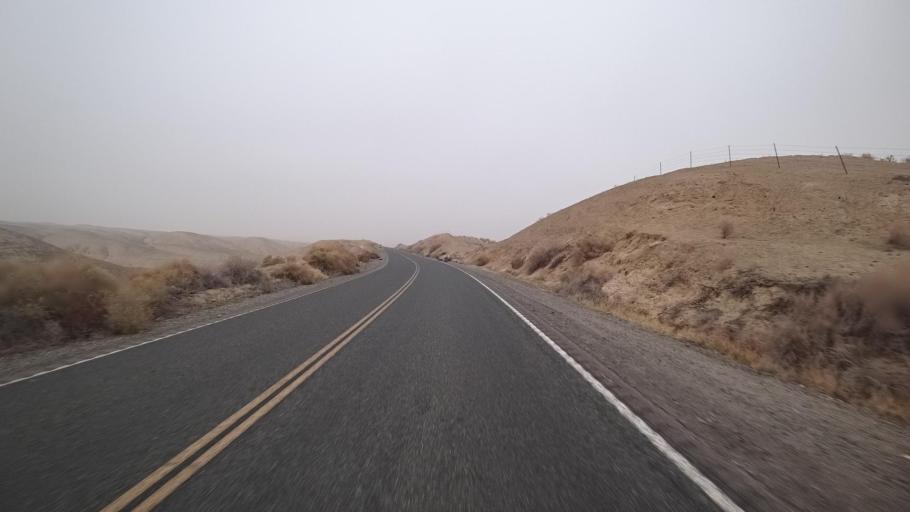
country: US
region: California
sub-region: Kern County
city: Buttonwillow
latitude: 35.3220
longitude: -119.4652
